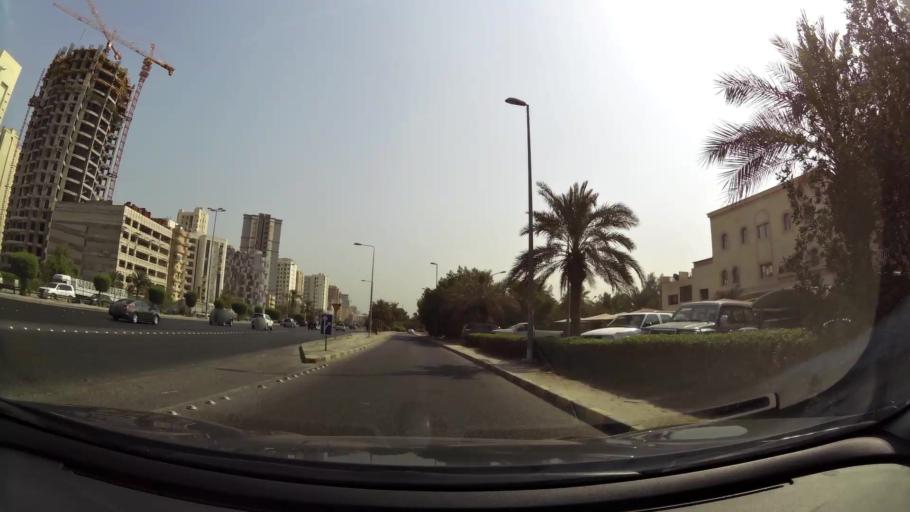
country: KW
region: Al Asimah
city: Ad Dasmah
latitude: 29.3555
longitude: 48.0227
